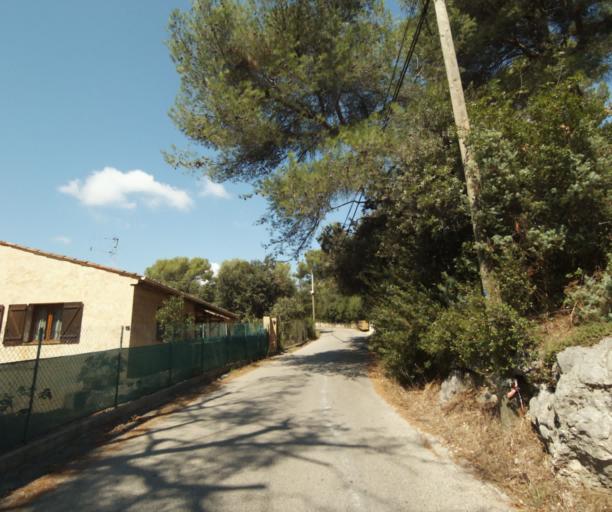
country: FR
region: Provence-Alpes-Cote d'Azur
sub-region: Departement des Alpes-Maritimes
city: Drap
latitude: 43.7562
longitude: 7.3388
